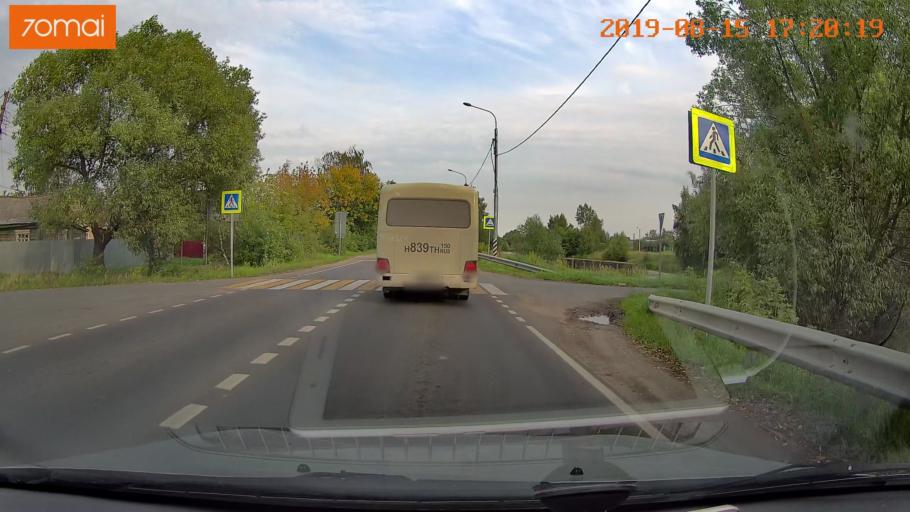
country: RU
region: Moskovskaya
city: Ashitkovo
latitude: 55.4247
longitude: 38.5579
